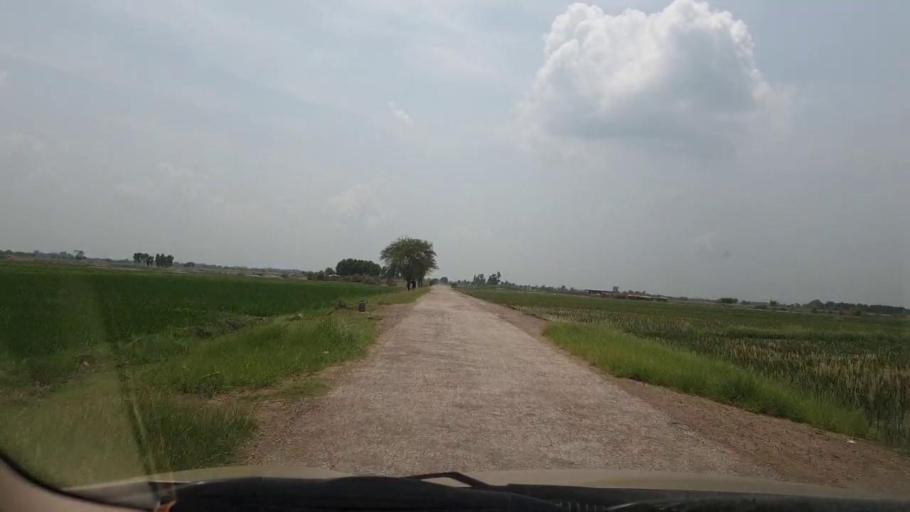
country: PK
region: Sindh
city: Larkana
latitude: 27.6218
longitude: 68.1469
